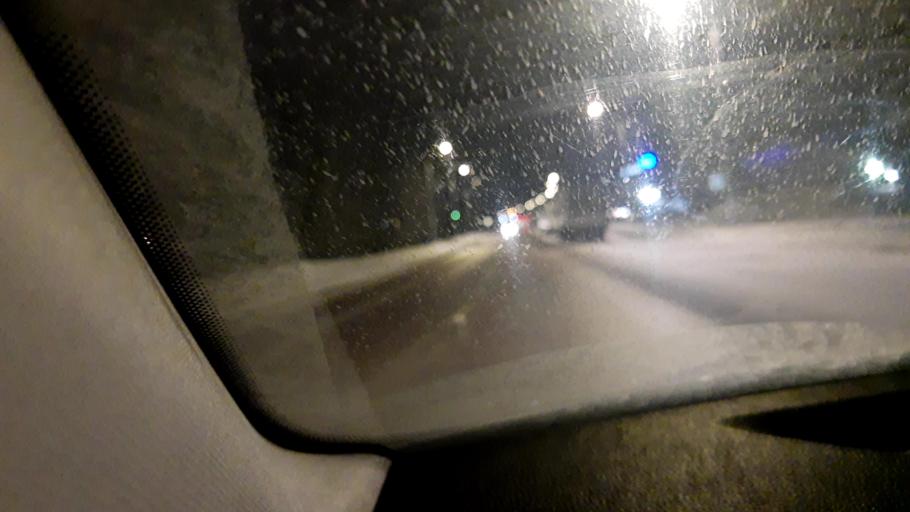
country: RU
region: Moskovskaya
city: Peresvet
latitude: 56.4450
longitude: 38.0986
